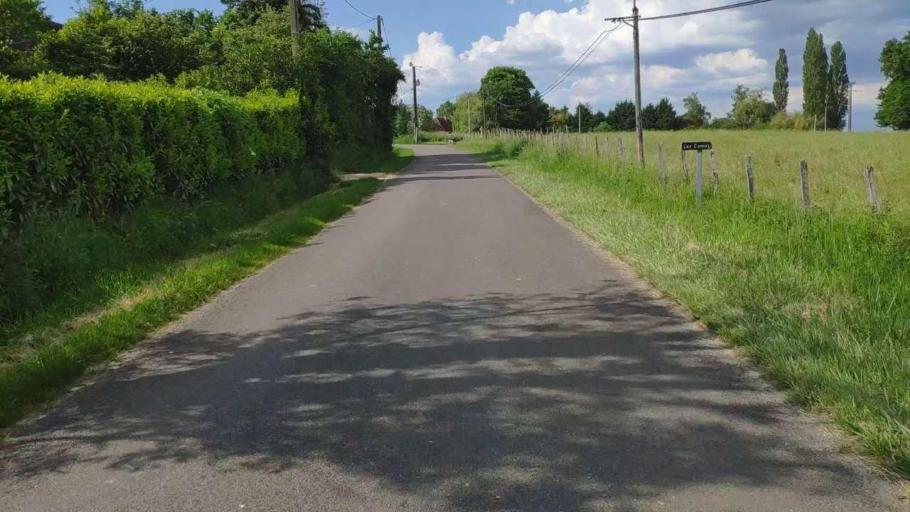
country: FR
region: Franche-Comte
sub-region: Departement du Jura
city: Bletterans
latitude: 46.8068
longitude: 5.3790
